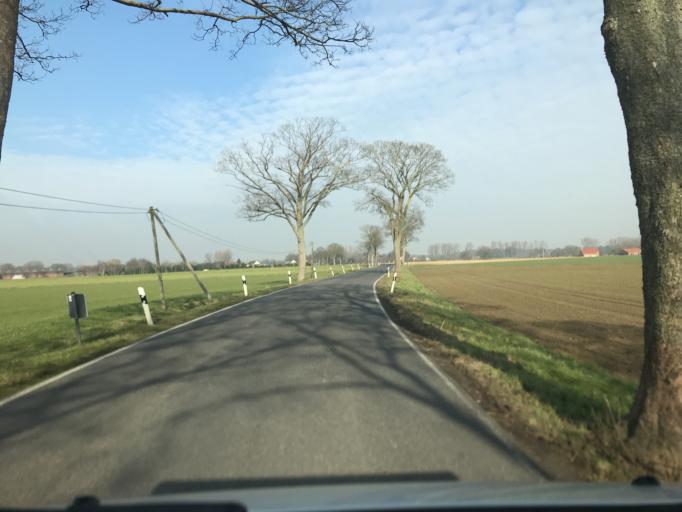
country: DE
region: North Rhine-Westphalia
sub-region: Regierungsbezirk Dusseldorf
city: Viersen
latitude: 51.2983
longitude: 6.3871
